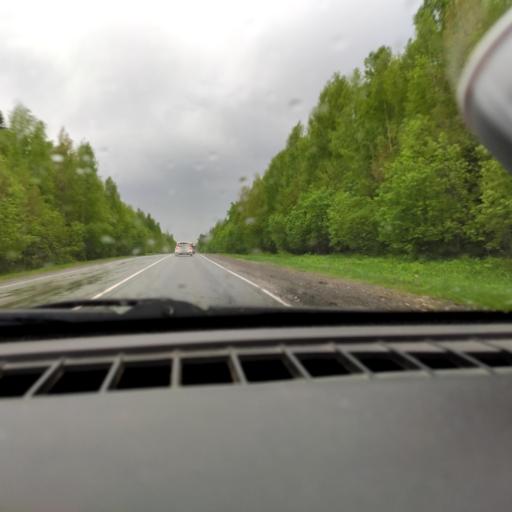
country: RU
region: Perm
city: Perm
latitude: 58.1735
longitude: 56.2321
